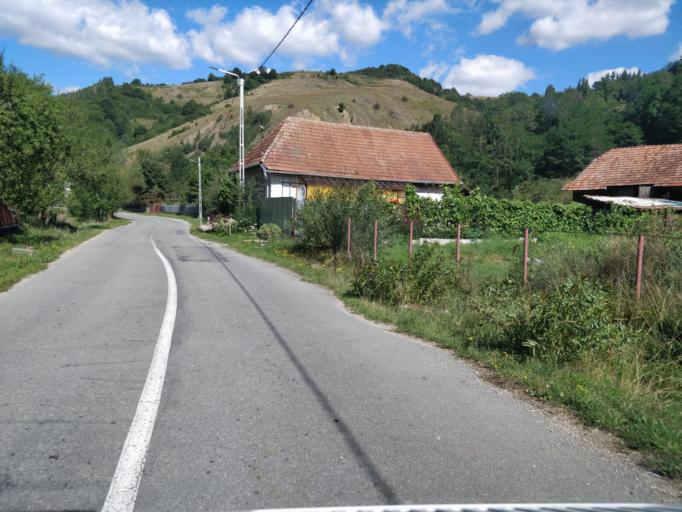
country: RO
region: Cluj
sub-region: Comuna Sacueu
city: Sacuieu
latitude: 46.8270
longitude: 22.8829
